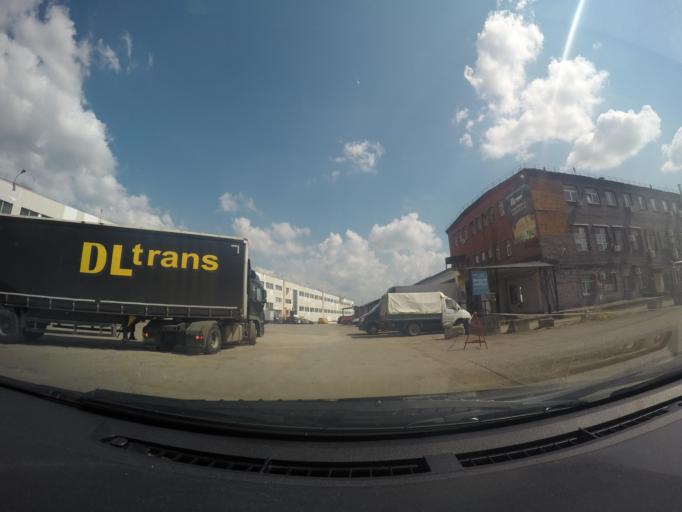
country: RU
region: Moscow
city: Novovladykino
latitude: 55.8491
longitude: 37.5987
